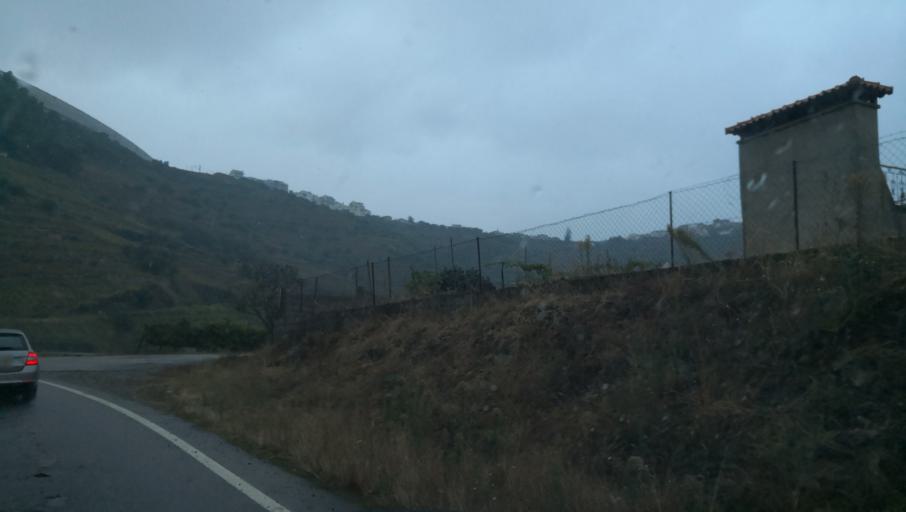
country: PT
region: Vila Real
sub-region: Santa Marta de Penaguiao
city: Santa Marta de Penaguiao
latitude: 41.2192
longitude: -7.7305
